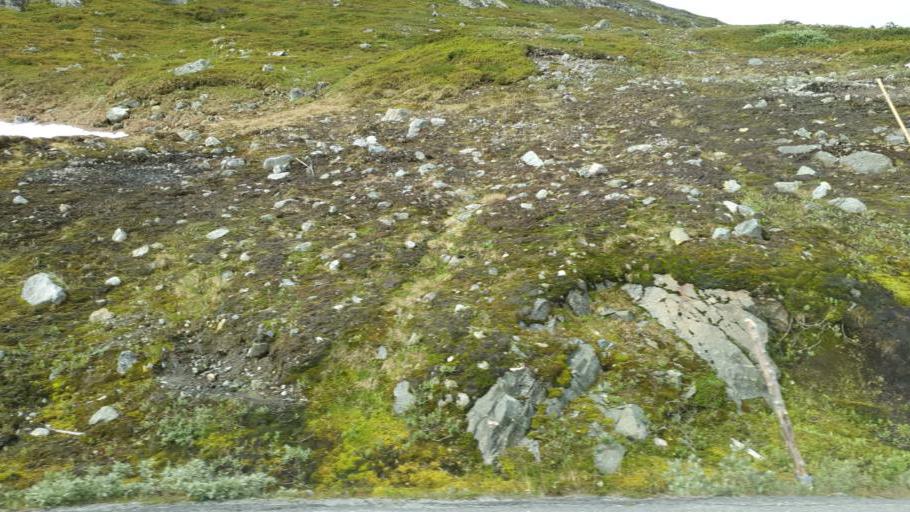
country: NO
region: Oppland
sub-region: Vestre Slidre
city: Slidre
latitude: 61.3420
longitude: 8.8127
